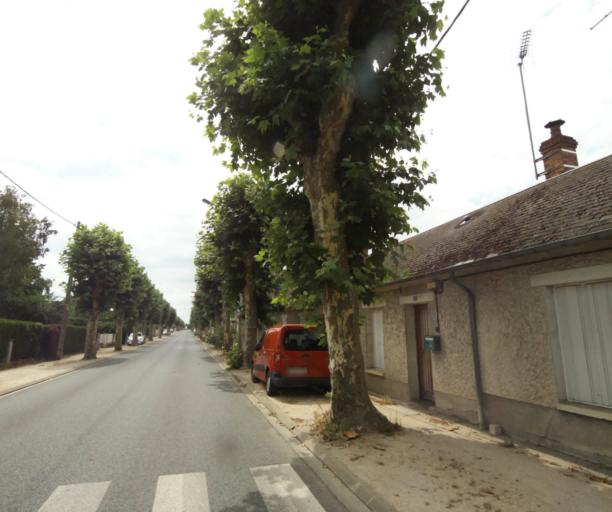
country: FR
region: Centre
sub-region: Departement du Loiret
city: Semoy
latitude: 47.9411
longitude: 1.9430
